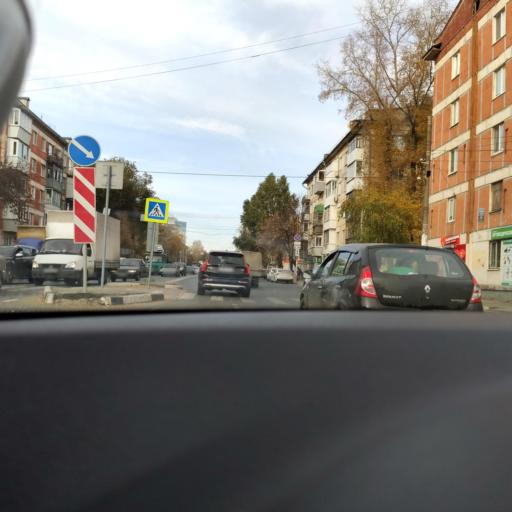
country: RU
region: Samara
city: Samara
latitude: 53.2008
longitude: 50.1902
